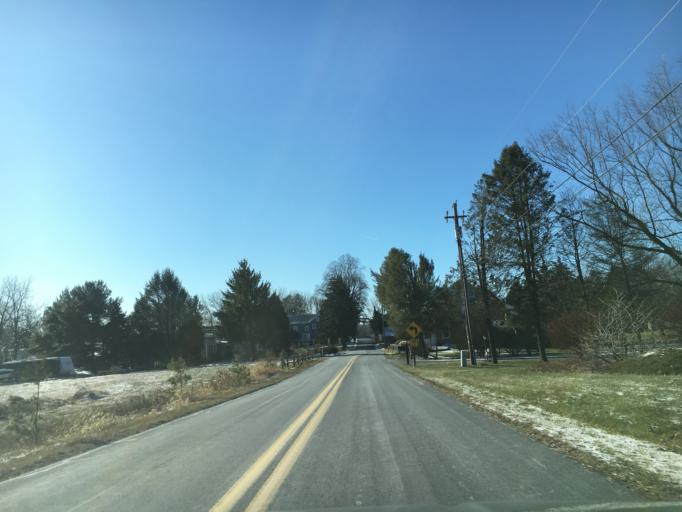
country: US
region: Pennsylvania
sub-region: Lehigh County
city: Egypt
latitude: 40.6837
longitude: -75.5691
